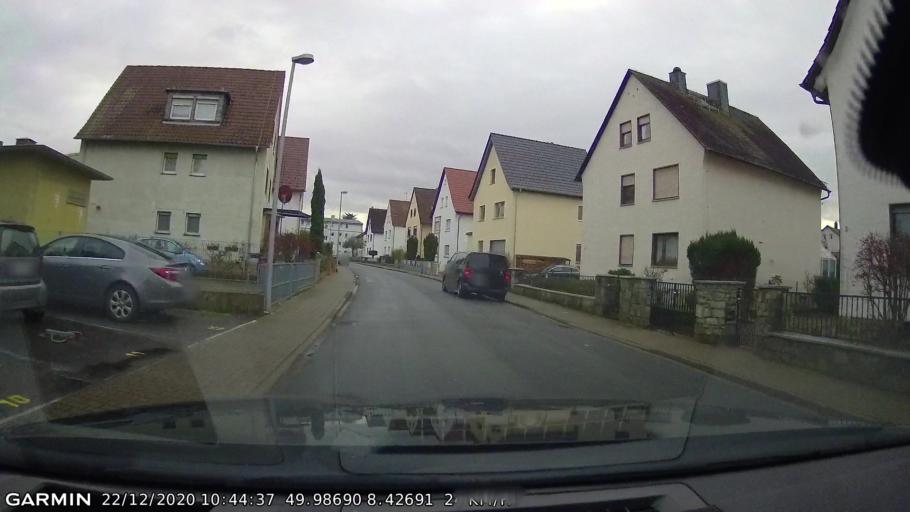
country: DE
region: Hesse
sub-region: Regierungsbezirk Darmstadt
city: Russelsheim
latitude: 49.9868
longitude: 8.4270
